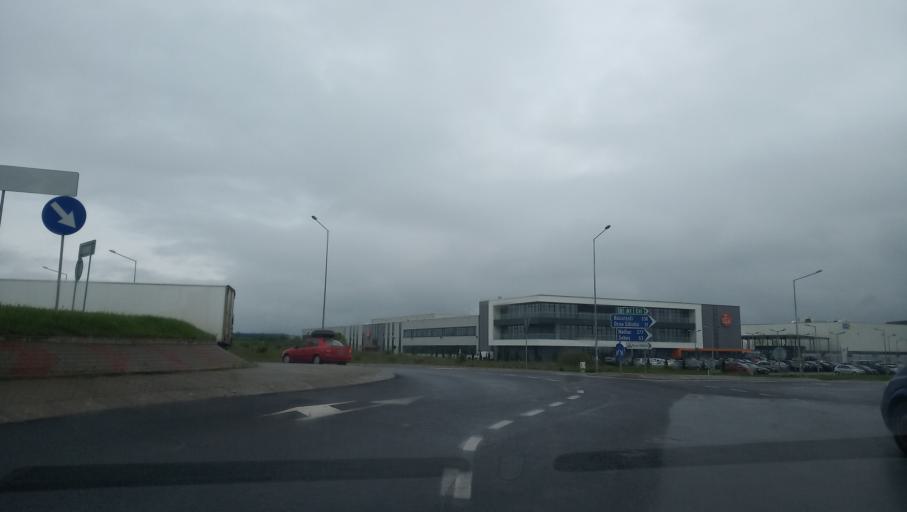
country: RO
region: Sibiu
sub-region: Comuna Cristian
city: Cristian
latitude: 45.7886
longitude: 24.0783
